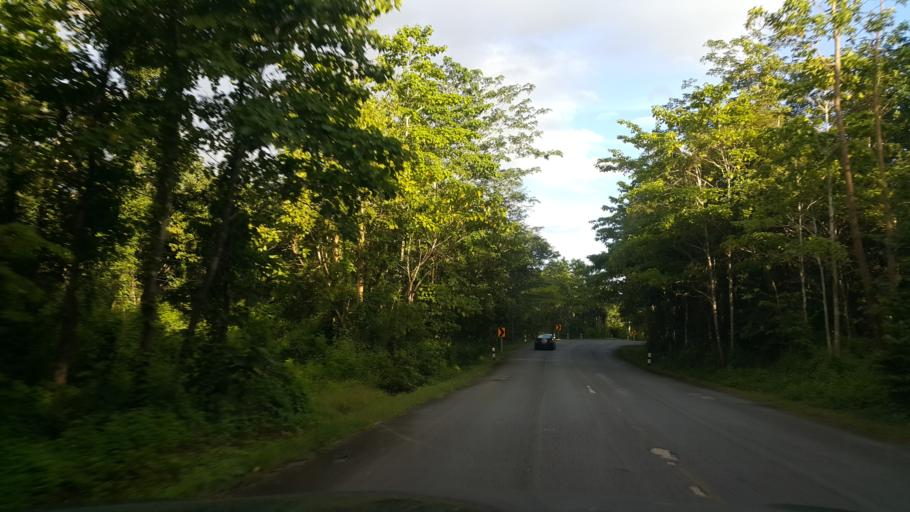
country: TH
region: Sukhothai
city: Thung Saliam
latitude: 17.4348
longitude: 99.3726
